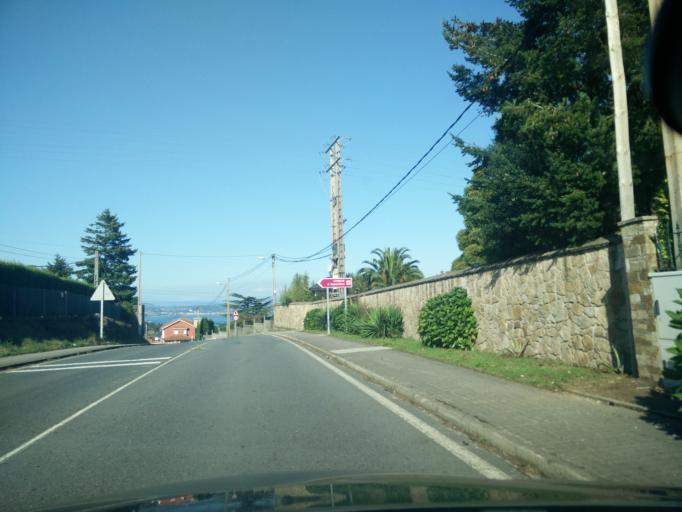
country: ES
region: Galicia
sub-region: Provincia da Coruna
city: Culleredo
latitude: 43.3243
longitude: -8.4069
